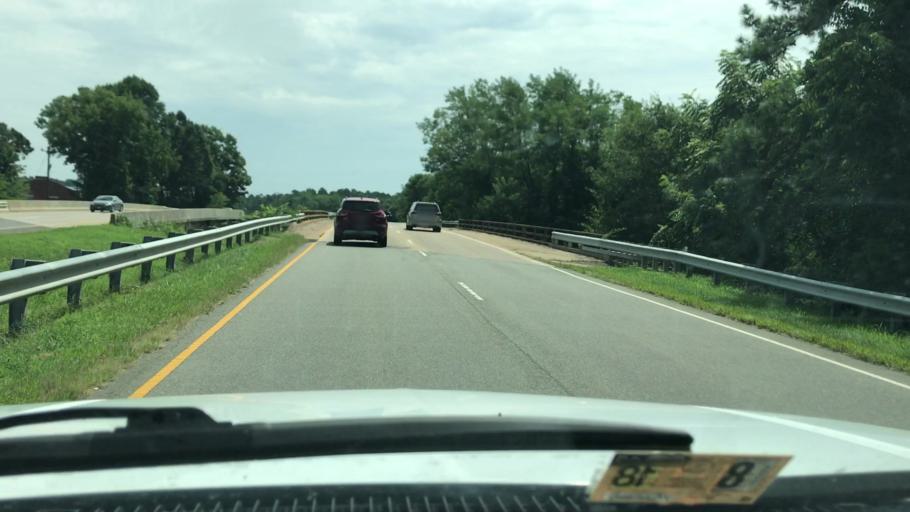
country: US
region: Virginia
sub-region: Chesterfield County
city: Brandermill
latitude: 37.5072
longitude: -77.6736
